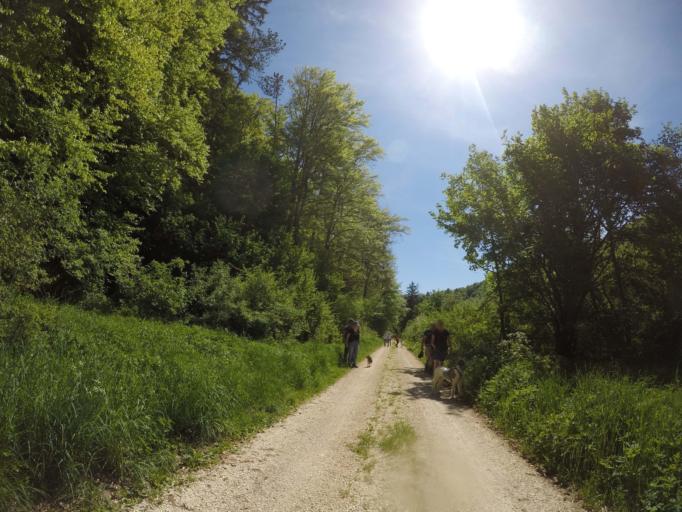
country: DE
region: Baden-Wuerttemberg
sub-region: Tuebingen Region
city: Blaubeuren
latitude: 48.3946
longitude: 9.7607
